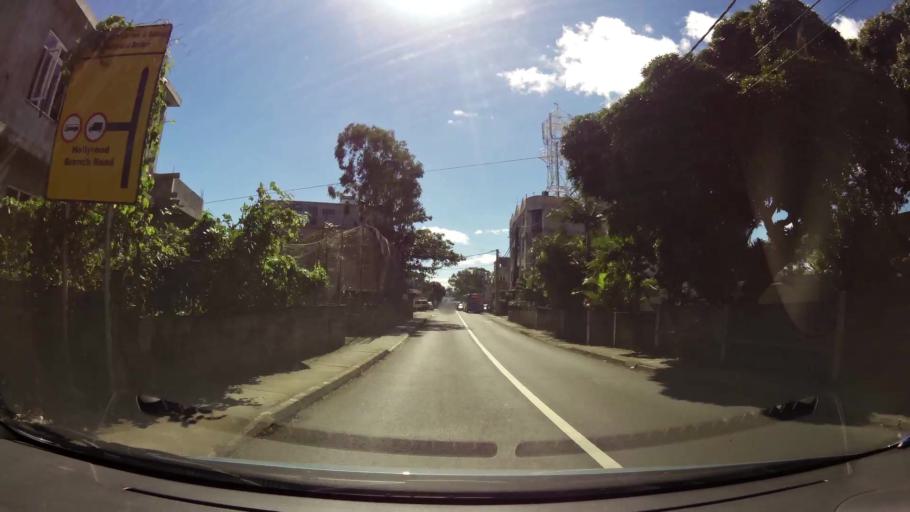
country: MU
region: Plaines Wilhems
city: Vacoas
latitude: -20.3138
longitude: 57.4849
